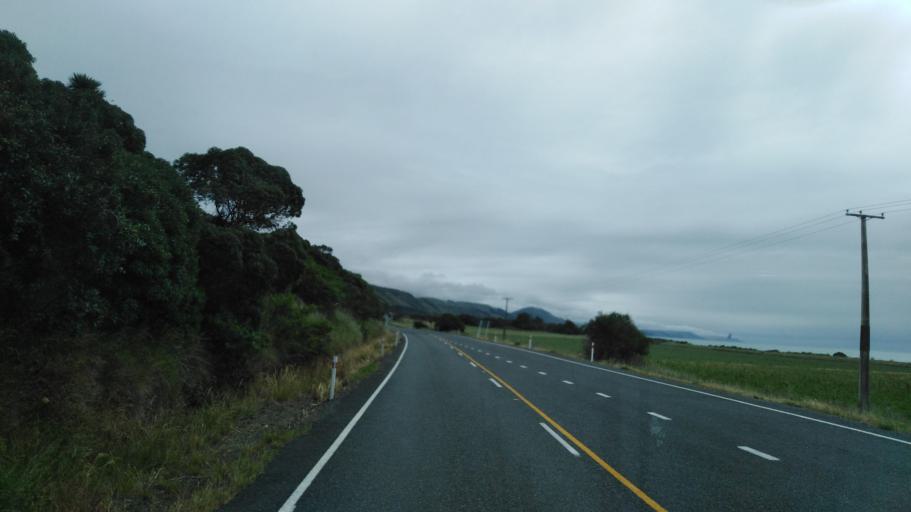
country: NZ
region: Canterbury
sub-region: Kaikoura District
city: Kaikoura
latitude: -42.1232
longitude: 173.9221
